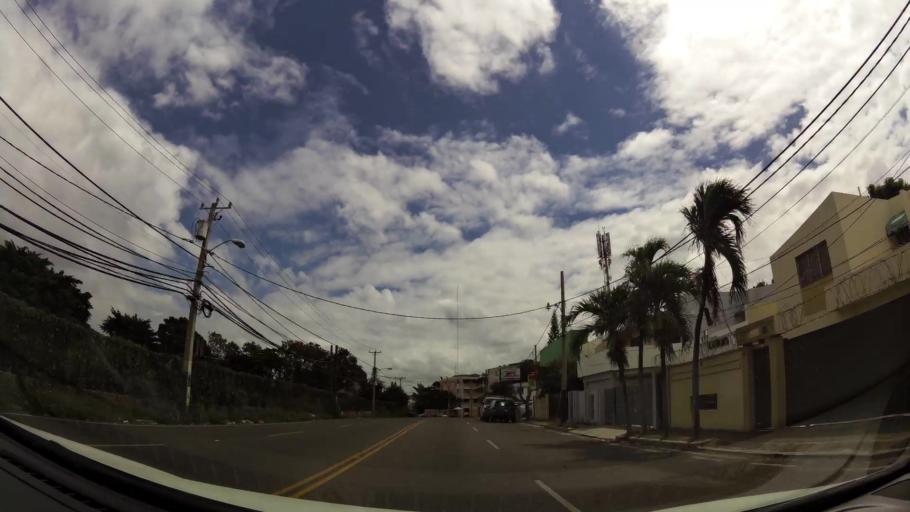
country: DO
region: Nacional
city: Bella Vista
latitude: 18.4697
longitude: -69.9662
